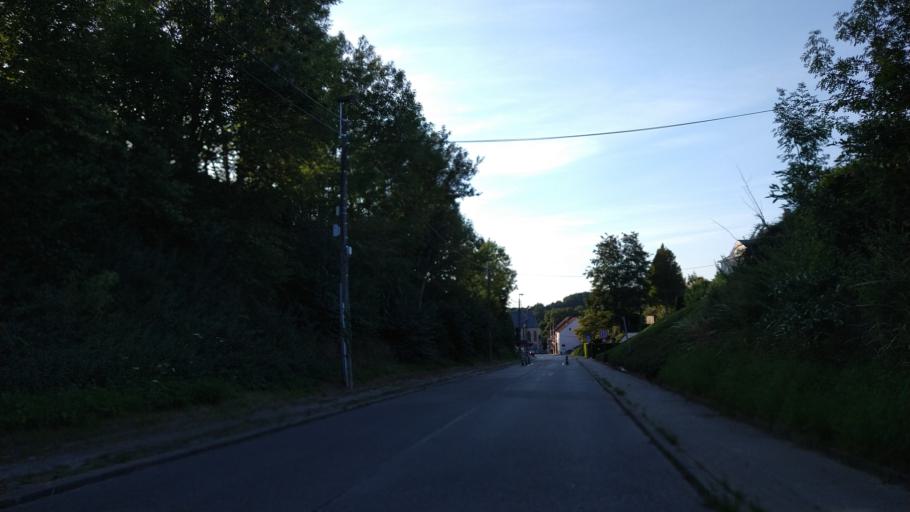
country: BE
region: Flanders
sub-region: Provincie Vlaams-Brabant
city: Bertem
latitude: 50.8456
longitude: 4.5935
